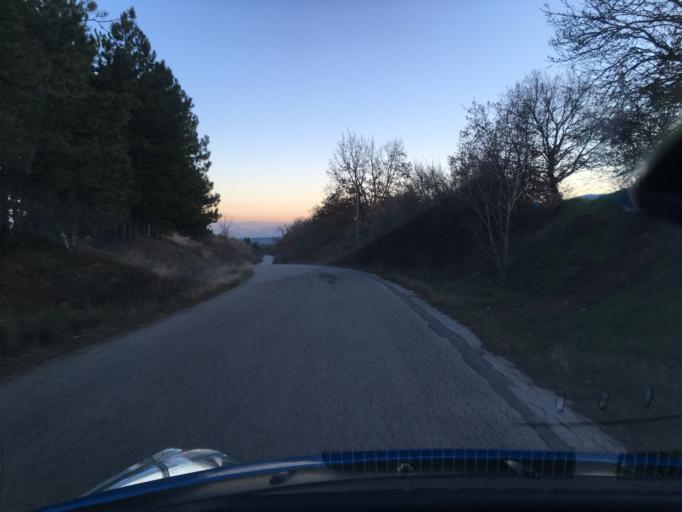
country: GR
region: West Macedonia
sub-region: Nomos Kozanis
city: Kozani
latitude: 40.2653
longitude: 21.7464
